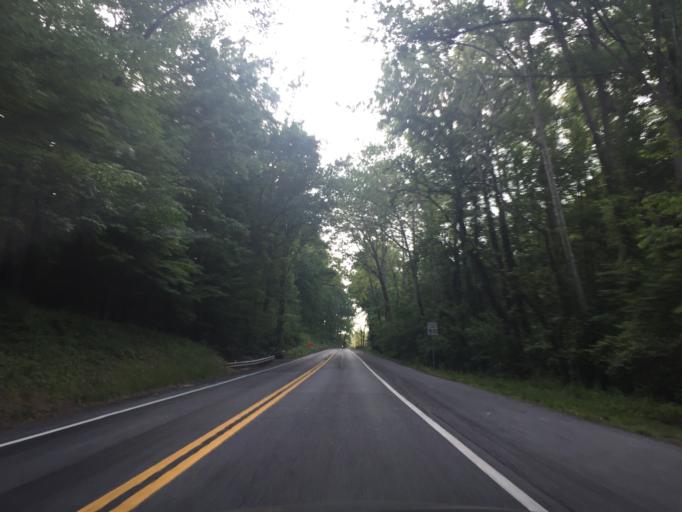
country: US
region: Maryland
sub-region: Frederick County
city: Point of Rocks
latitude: 39.2882
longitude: -77.5340
